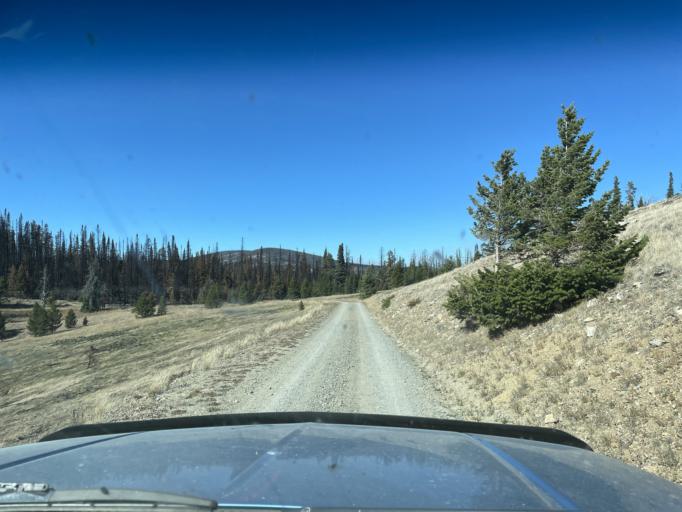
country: US
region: Montana
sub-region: Broadwater County
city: Townsend
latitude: 46.4980
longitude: -111.2580
